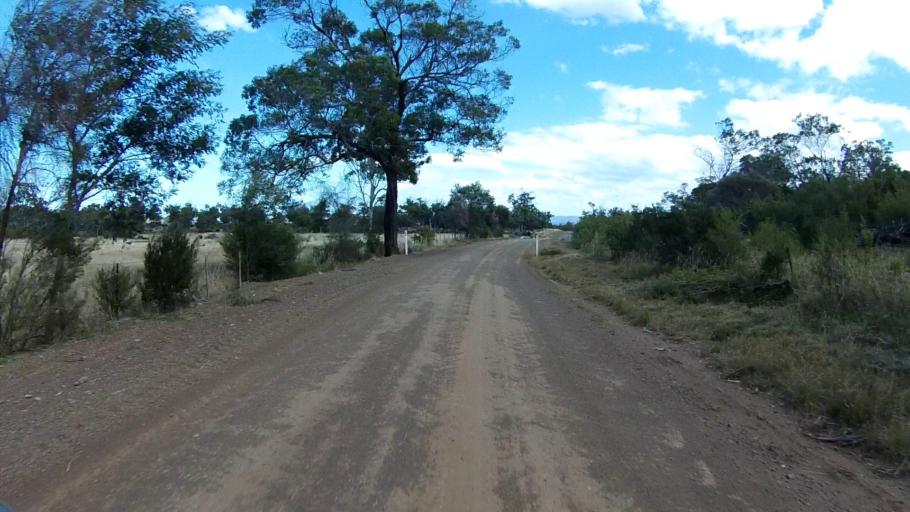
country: AU
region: Tasmania
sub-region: Break O'Day
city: St Helens
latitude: -41.9781
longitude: 148.0692
